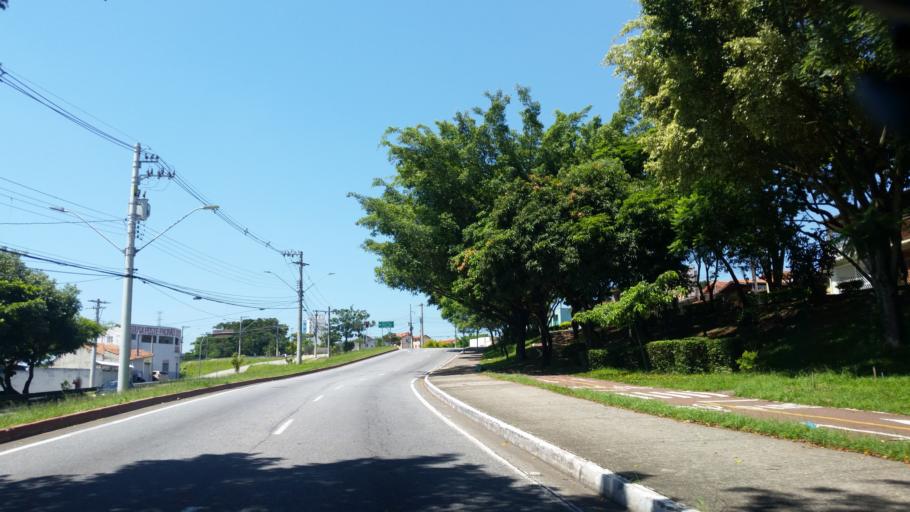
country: BR
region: Sao Paulo
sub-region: Sao Jose Dos Campos
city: Sao Jose dos Campos
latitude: -23.1716
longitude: -45.8122
